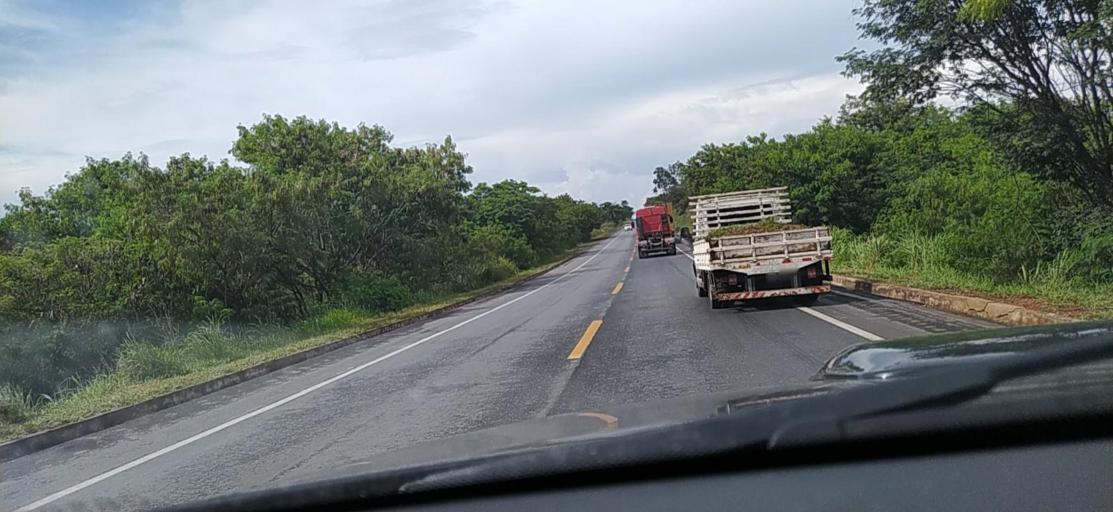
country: BR
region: Minas Gerais
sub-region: Montes Claros
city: Montes Claros
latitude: -16.8548
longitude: -43.8527
